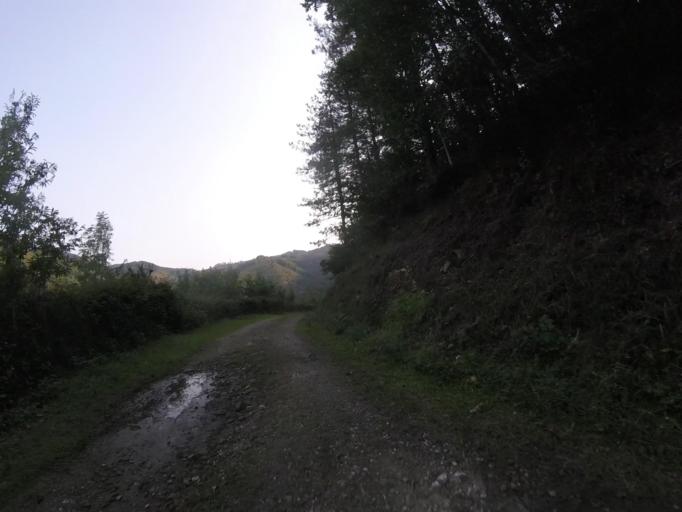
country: ES
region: Basque Country
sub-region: Provincia de Guipuzcoa
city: Errenteria
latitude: 43.2629
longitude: -1.8458
